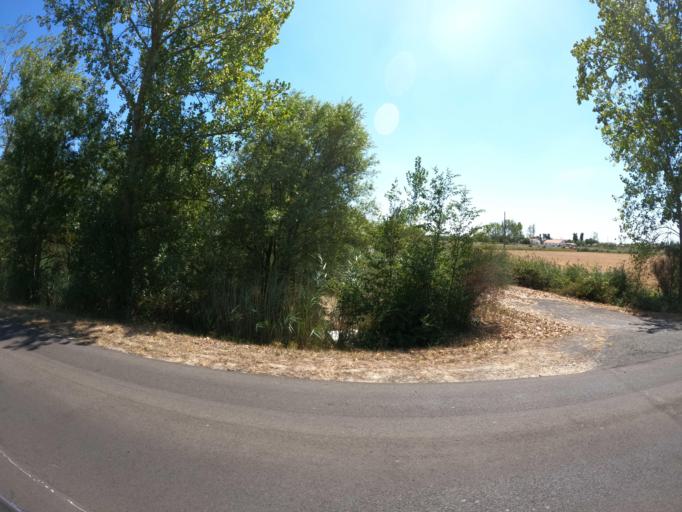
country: FR
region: Pays de la Loire
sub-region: Departement de la Vendee
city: Sallertaine
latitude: 46.8269
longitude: -1.9511
